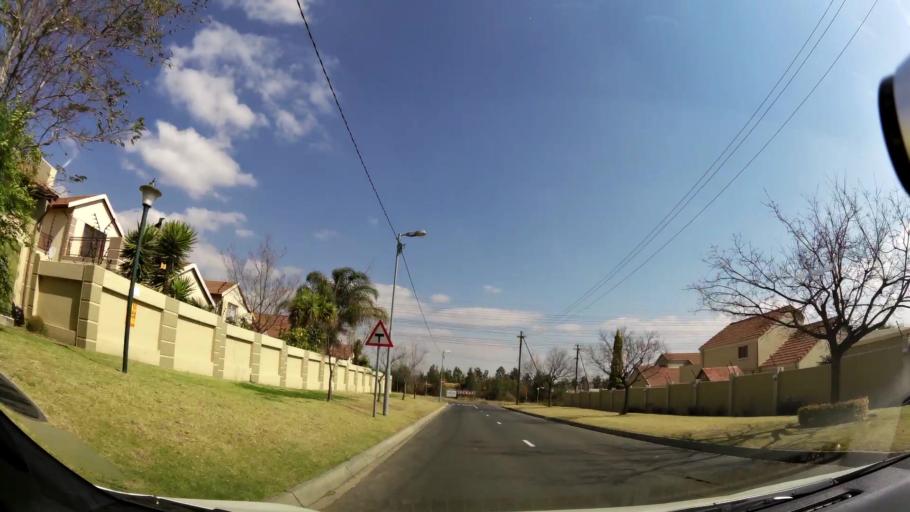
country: ZA
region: Gauteng
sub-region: City of Johannesburg Metropolitan Municipality
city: Midrand
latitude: -26.0128
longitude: 28.0722
